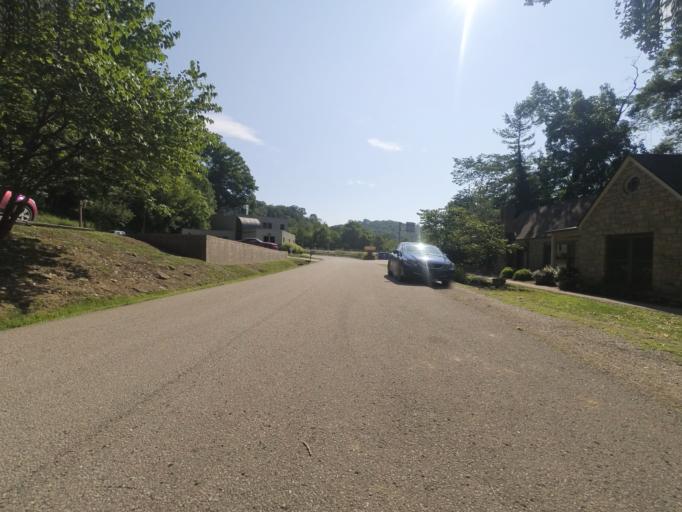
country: US
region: West Virginia
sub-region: Cabell County
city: Huntington
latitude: 38.3962
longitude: -82.4516
